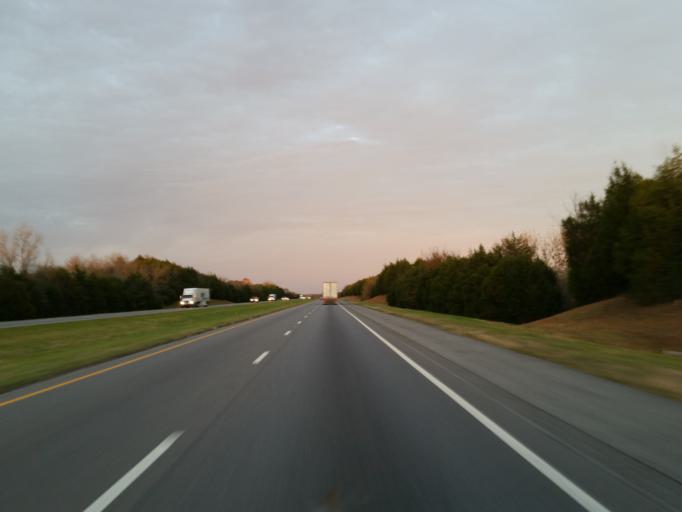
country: US
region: Alabama
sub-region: Sumter County
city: Livingston
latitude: 32.6572
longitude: -88.1853
